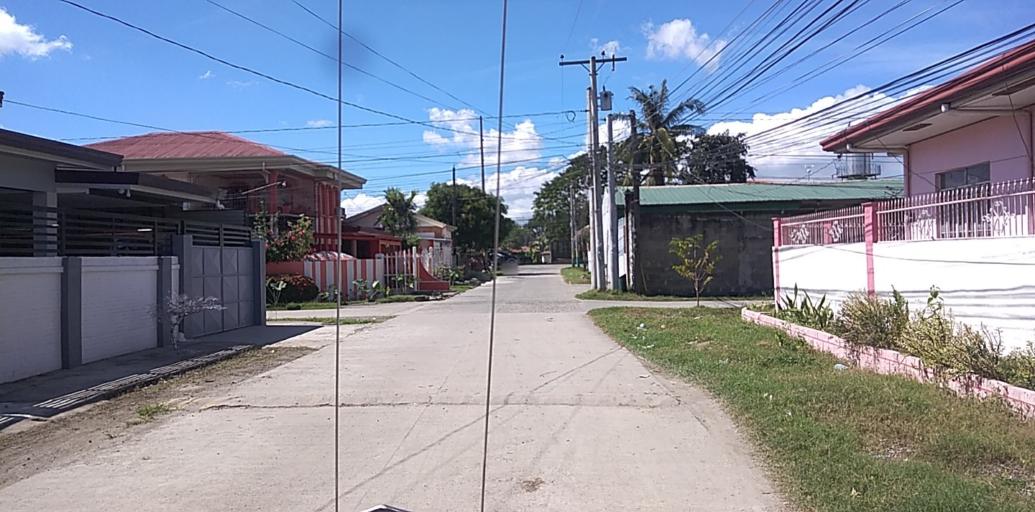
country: PH
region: Central Luzon
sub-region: Province of Pampanga
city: Arayat
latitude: 15.1378
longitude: 120.7742
